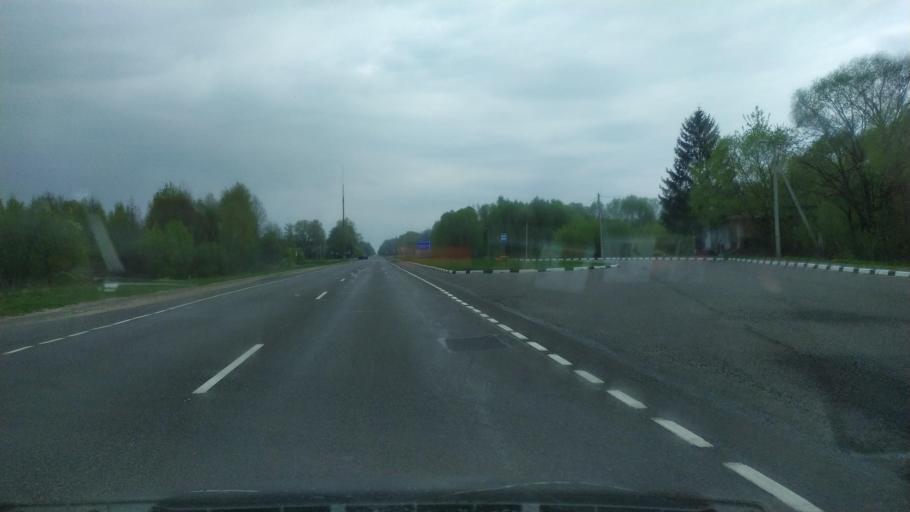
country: BY
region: Brest
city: Horad Kobryn
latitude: 52.3285
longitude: 24.5750
